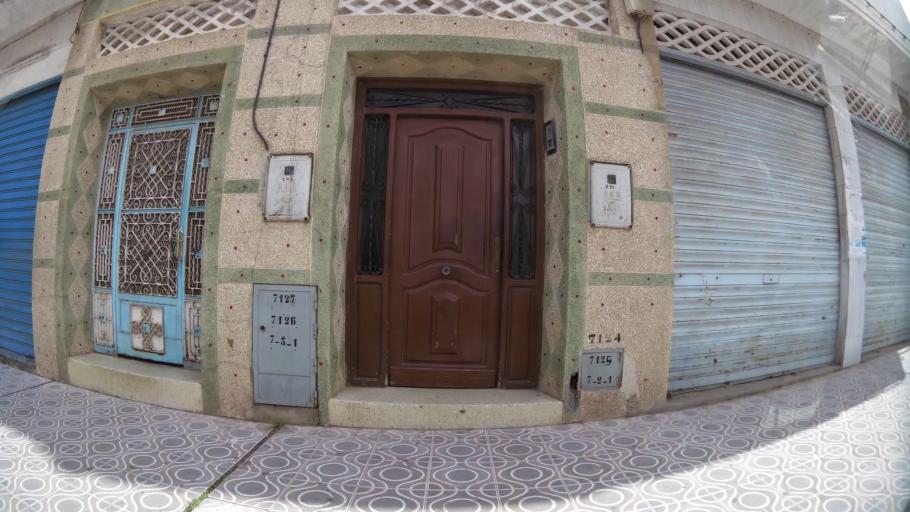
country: MA
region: Oriental
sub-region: Nador
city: Nador
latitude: 35.1741
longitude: -2.9339
